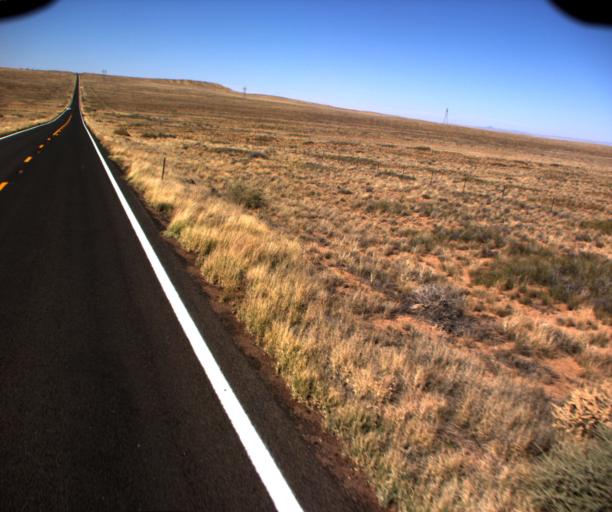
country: US
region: Arizona
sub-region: Coconino County
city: Tuba City
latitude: 35.9416
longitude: -110.9086
